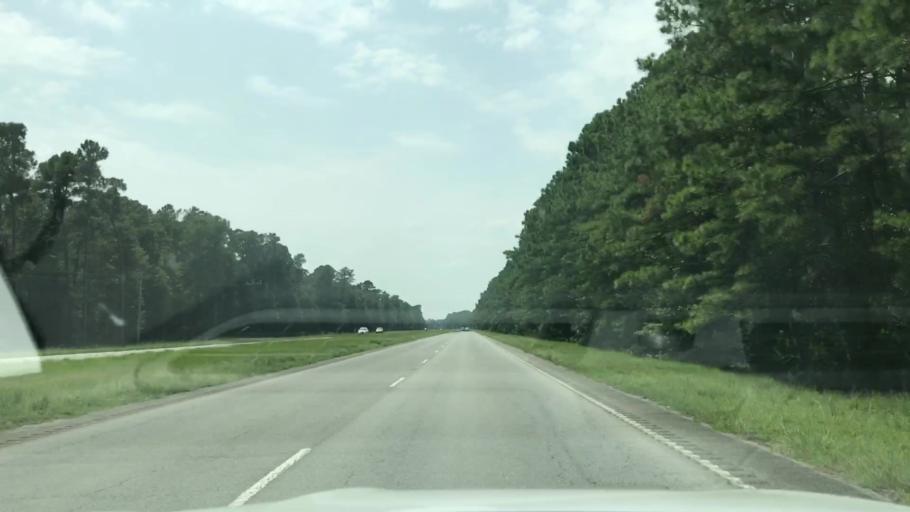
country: US
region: South Carolina
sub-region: Charleston County
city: Awendaw
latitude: 33.0660
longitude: -79.5295
